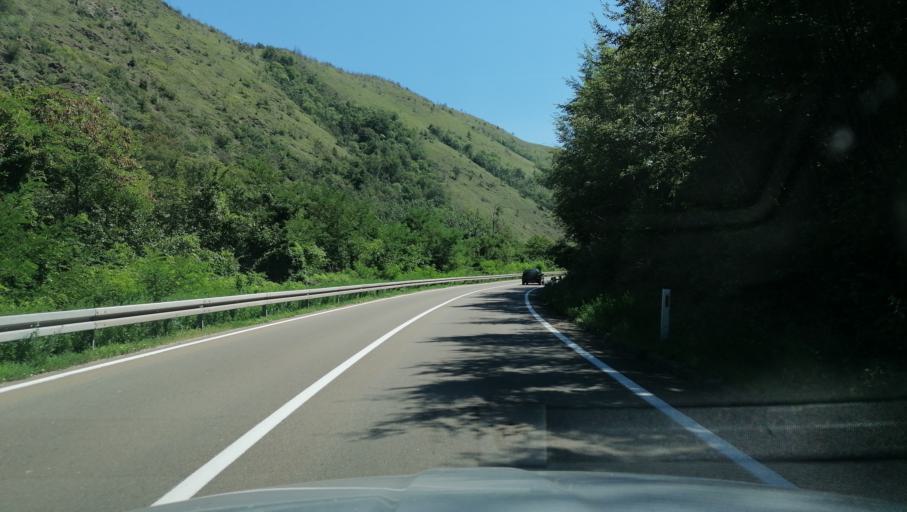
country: RS
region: Central Serbia
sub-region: Raski Okrug
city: Kraljevo
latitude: 43.5682
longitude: 20.6000
